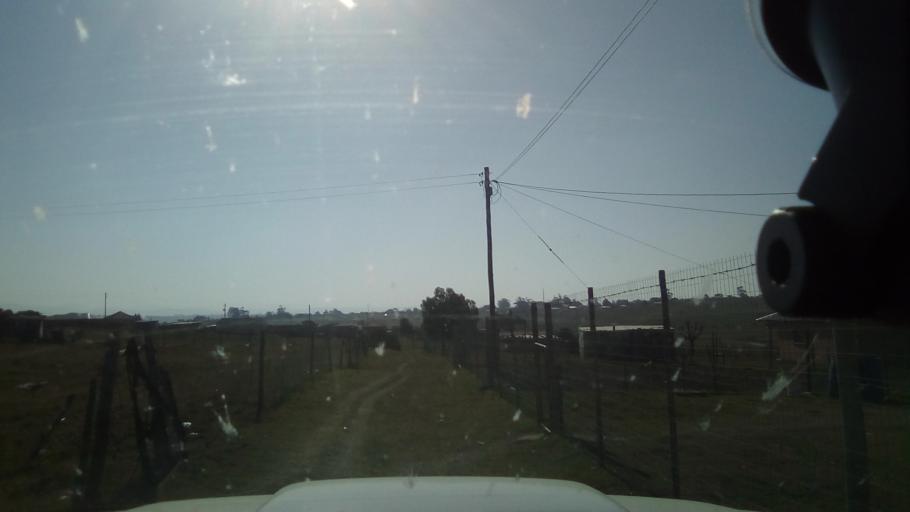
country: ZA
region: Eastern Cape
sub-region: Buffalo City Metropolitan Municipality
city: Bhisho
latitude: -32.9499
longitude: 27.3240
